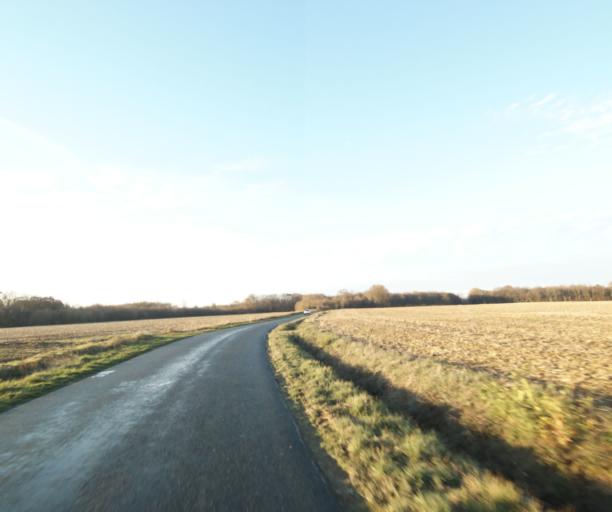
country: FR
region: Poitou-Charentes
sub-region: Departement de la Charente-Maritime
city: Nieul-les-Saintes
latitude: 45.7984
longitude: -0.7461
